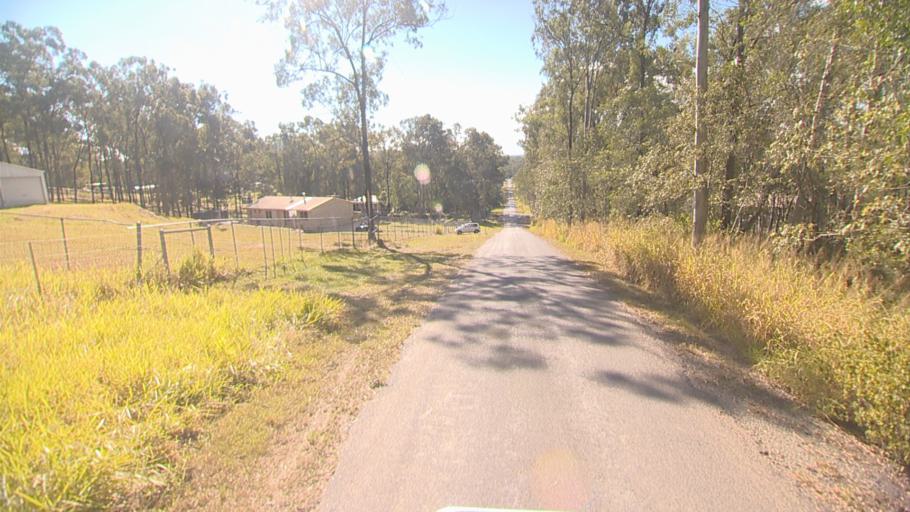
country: AU
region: Queensland
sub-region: Logan
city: Chambers Flat
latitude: -27.8108
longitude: 153.0818
